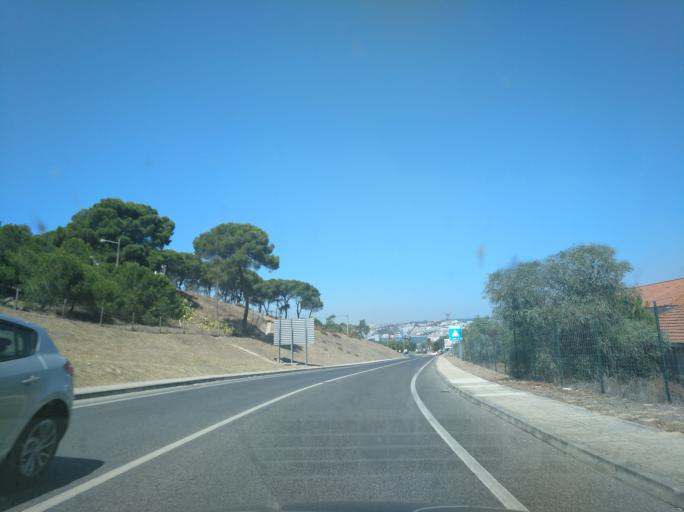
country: PT
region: Setubal
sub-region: Almada
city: Trafaria
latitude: 38.6674
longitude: -9.2326
